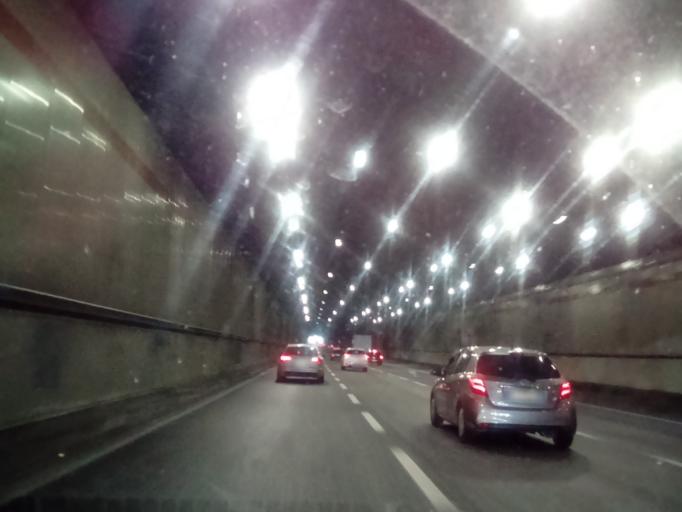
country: IT
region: Latium
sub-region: Citta metropolitana di Roma Capitale
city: Borgo Lotti
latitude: 41.8054
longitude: 12.5606
